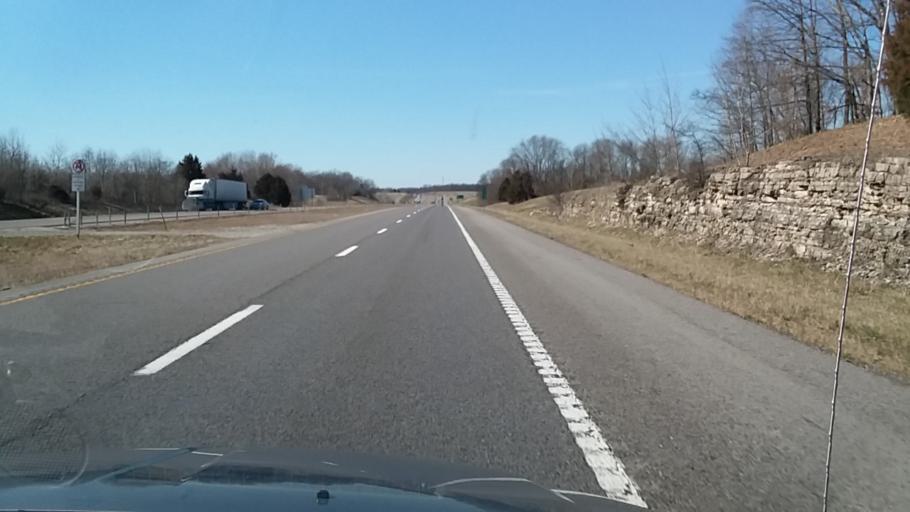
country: US
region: Missouri
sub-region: Perry County
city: Perryville
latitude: 37.5861
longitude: -89.7676
